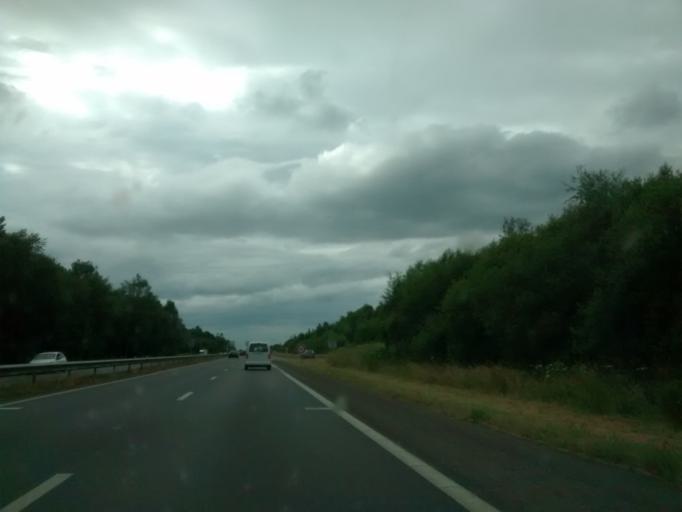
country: FR
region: Brittany
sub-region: Departement des Cotes-d'Armor
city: Plestan
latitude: 48.4055
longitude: -2.4158
